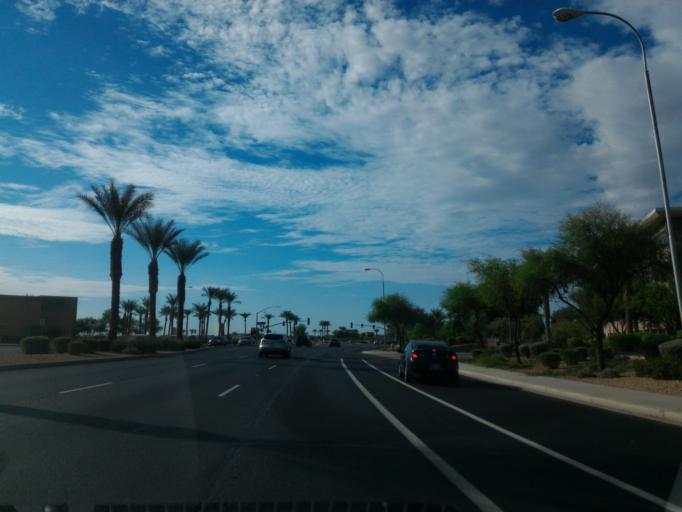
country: US
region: Arizona
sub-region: Maricopa County
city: Chandler
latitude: 33.2886
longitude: -111.8914
